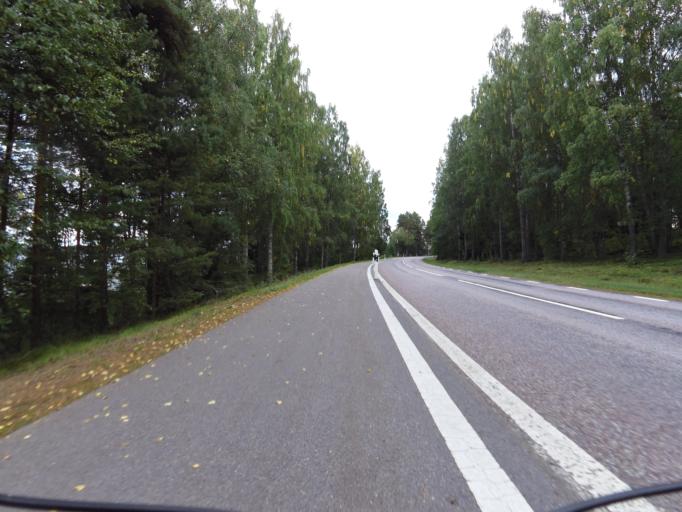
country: SE
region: Gaevleborg
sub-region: Sandvikens Kommun
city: Sandviken
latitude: 60.7007
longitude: 16.8165
